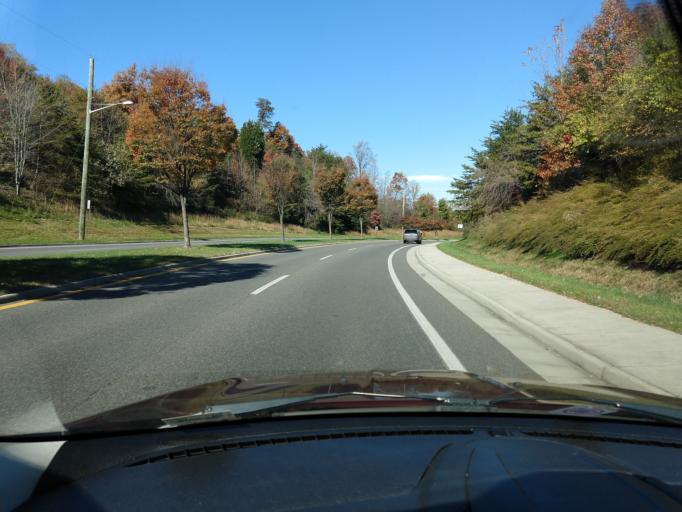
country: US
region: Virginia
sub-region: City of Salem
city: Salem
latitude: 37.2773
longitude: -80.0097
